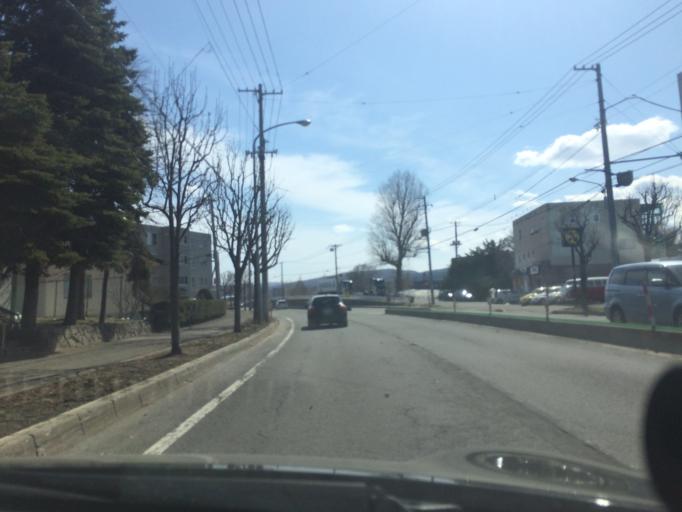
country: JP
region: Hokkaido
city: Sapporo
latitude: 42.9930
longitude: 141.4408
